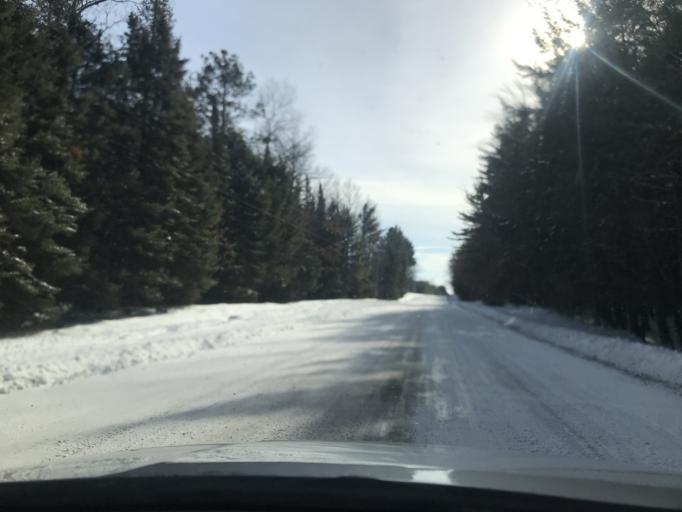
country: US
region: Wisconsin
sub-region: Oconto County
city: Gillett
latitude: 45.1346
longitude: -88.2497
